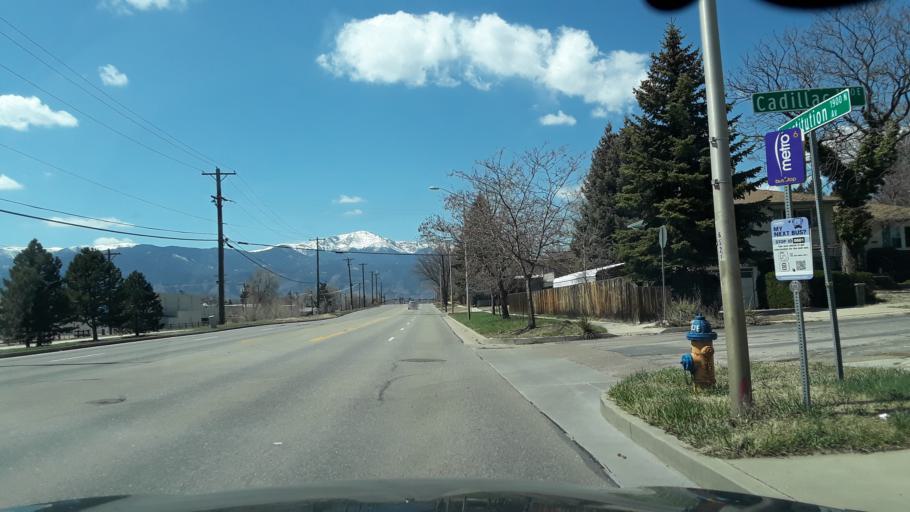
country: US
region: Colorado
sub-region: El Paso County
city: Colorado Springs
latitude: 38.8594
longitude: -104.7714
